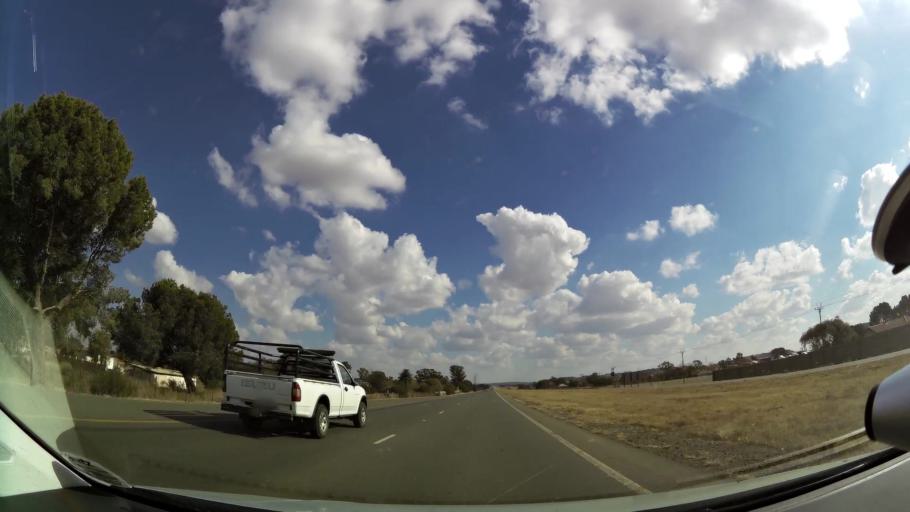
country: ZA
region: Orange Free State
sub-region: Mangaung Metropolitan Municipality
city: Bloemfontein
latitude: -29.1329
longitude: 26.1430
